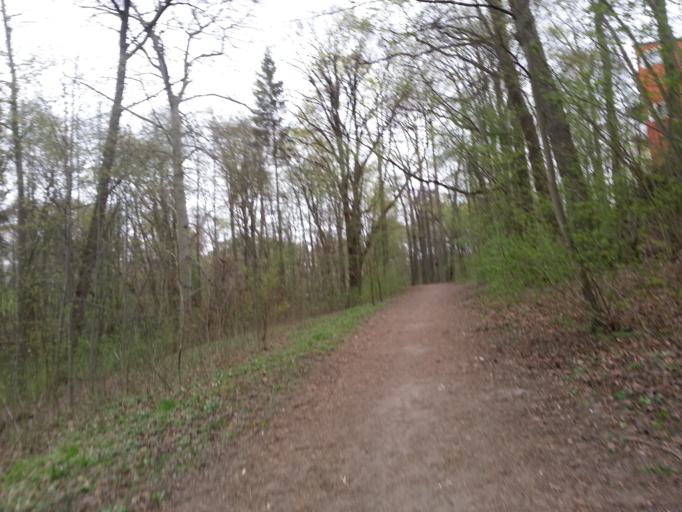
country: NO
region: Oslo
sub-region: Oslo
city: Sjolyststranda
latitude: 59.9257
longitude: 10.6886
